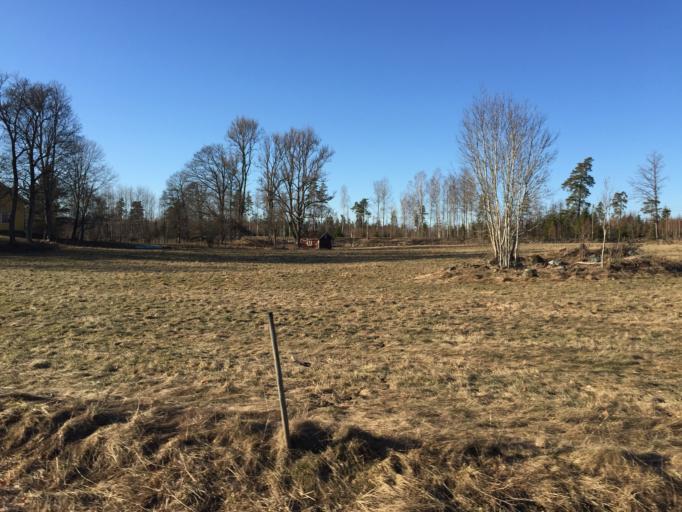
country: SE
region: Soedermanland
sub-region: Vingakers Kommun
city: Vingaker
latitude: 59.0459
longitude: 15.7657
